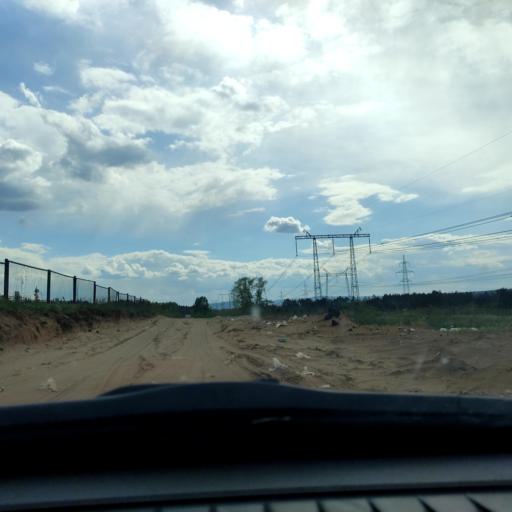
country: RU
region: Samara
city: Zhigulevsk
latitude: 53.5302
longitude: 49.5442
